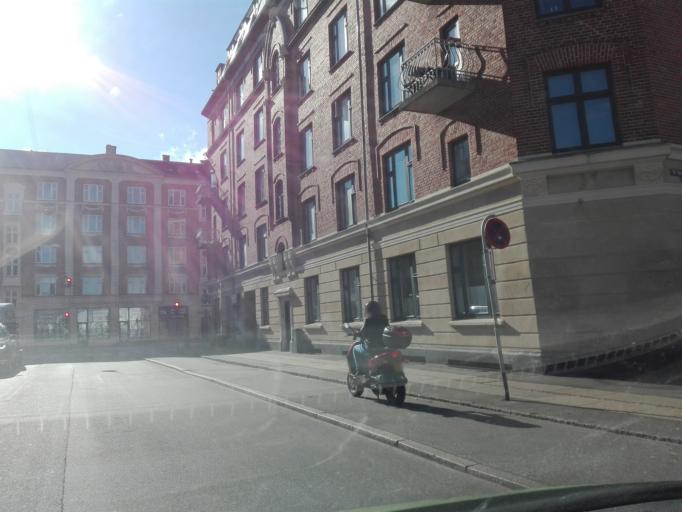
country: DK
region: Capital Region
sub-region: Kobenhavn
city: Christianshavn
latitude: 55.6671
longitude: 12.6125
